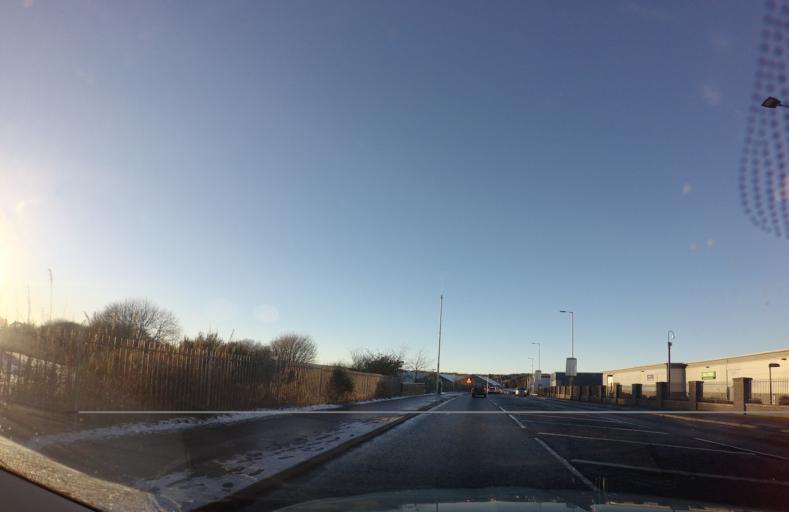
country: GB
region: Scotland
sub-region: Dundee City
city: Dundee
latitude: 56.4799
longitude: -2.9944
